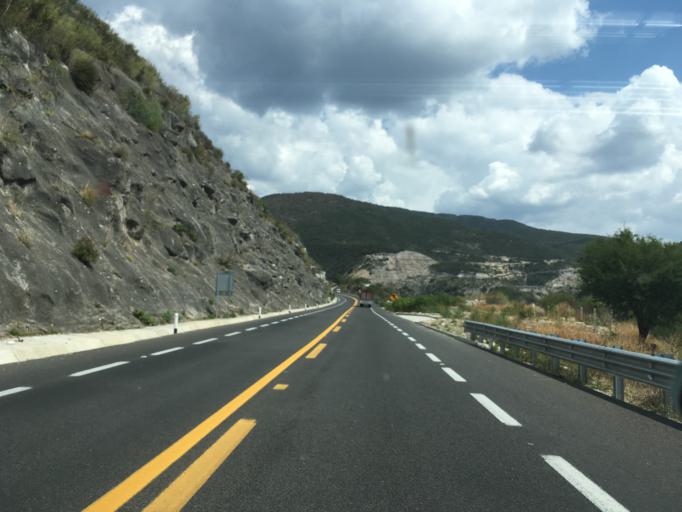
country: MX
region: Puebla
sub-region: San Jose Miahuatlan
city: San Pedro Tetitlan
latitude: 18.0323
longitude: -97.3499
